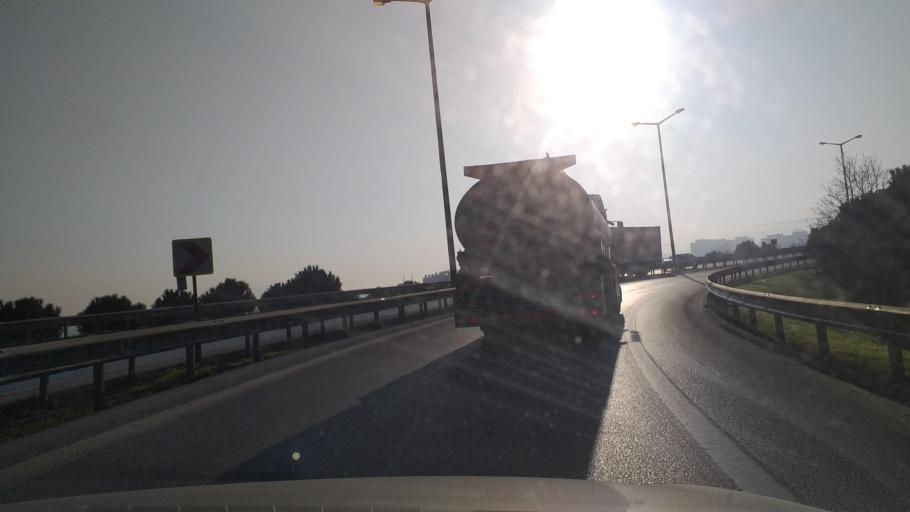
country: TR
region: Istanbul
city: Samandira
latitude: 40.9848
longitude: 29.2052
